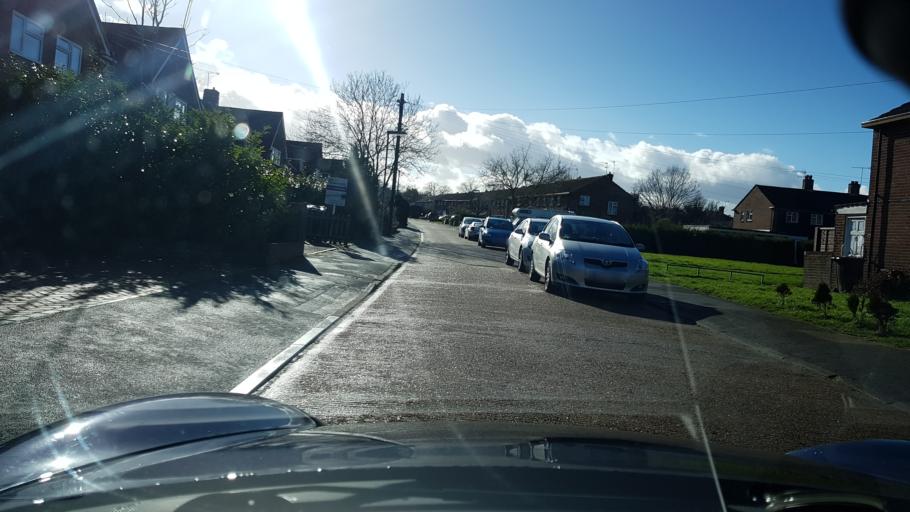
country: GB
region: England
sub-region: Surrey
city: Guildford
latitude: 51.2461
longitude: -0.6099
